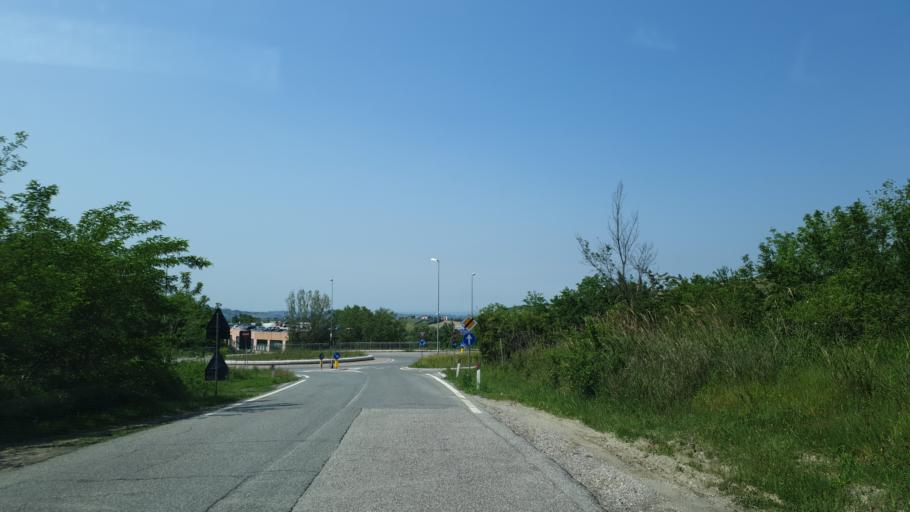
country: SM
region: Borgo Maggiore
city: Borgo Maggiore
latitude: 43.9423
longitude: 12.4330
